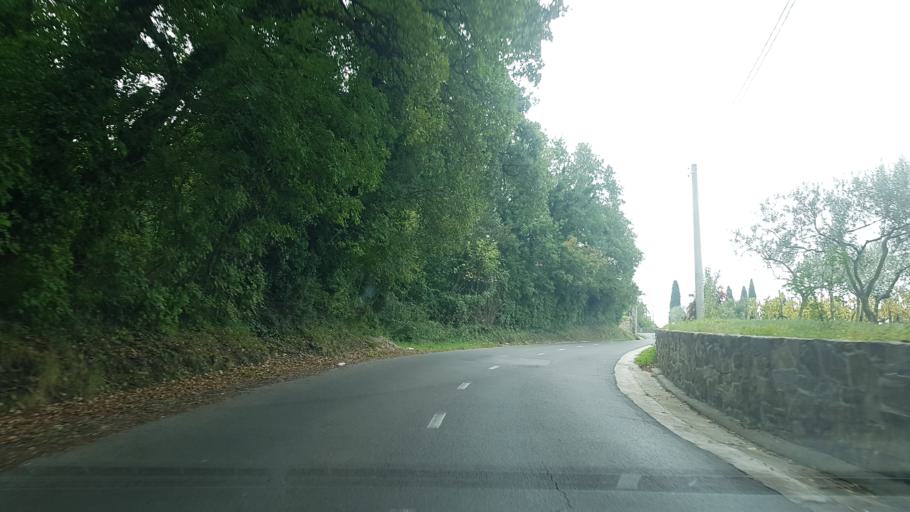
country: SI
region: Koper-Capodistria
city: Spodnje Skofije
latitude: 45.5791
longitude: 13.8045
